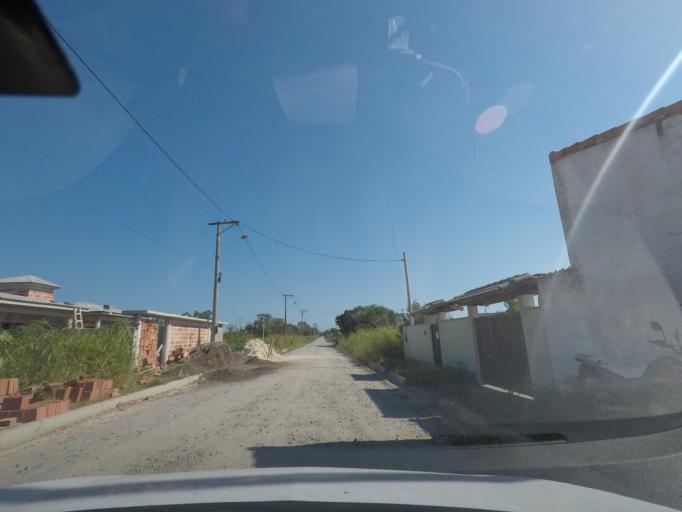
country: BR
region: Rio de Janeiro
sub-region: Marica
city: Marica
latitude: -22.9610
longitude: -42.9245
